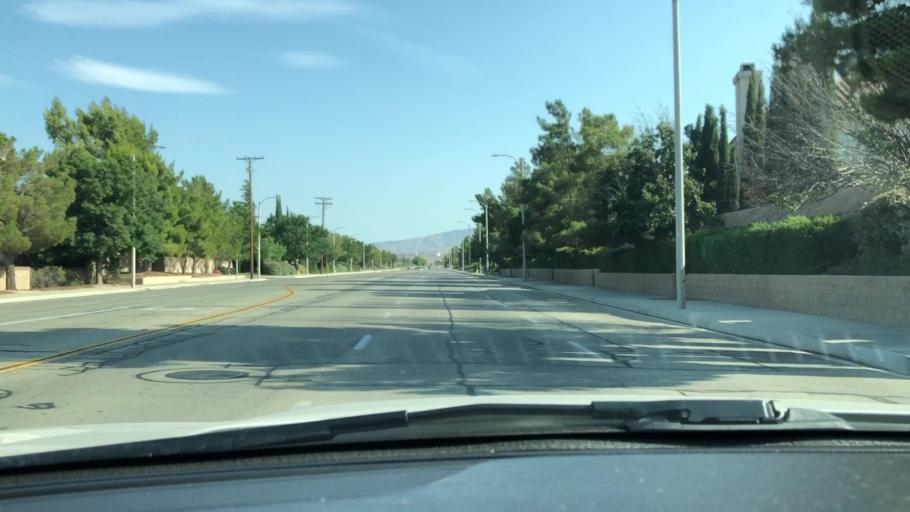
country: US
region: California
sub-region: Los Angeles County
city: Quartz Hill
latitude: 34.6867
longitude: -118.2016
